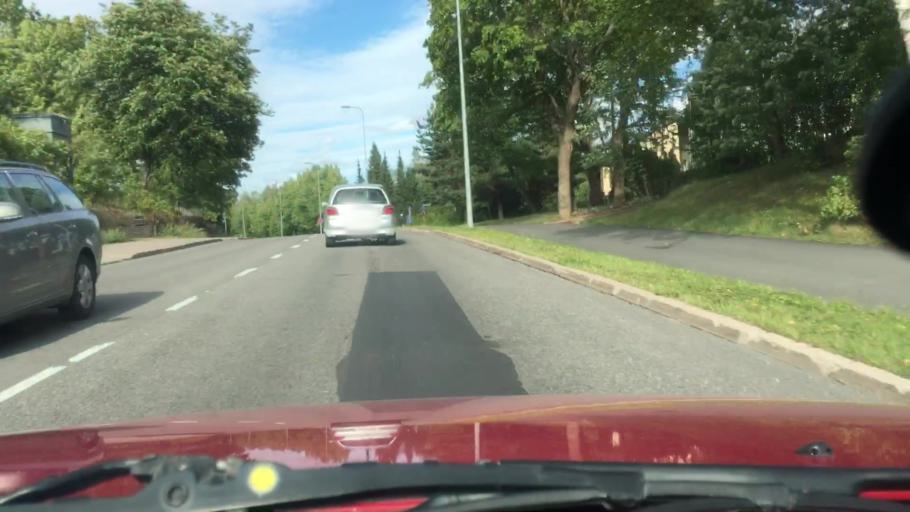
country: FI
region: Varsinais-Suomi
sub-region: Turku
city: Turku
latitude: 60.4555
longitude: 22.2432
